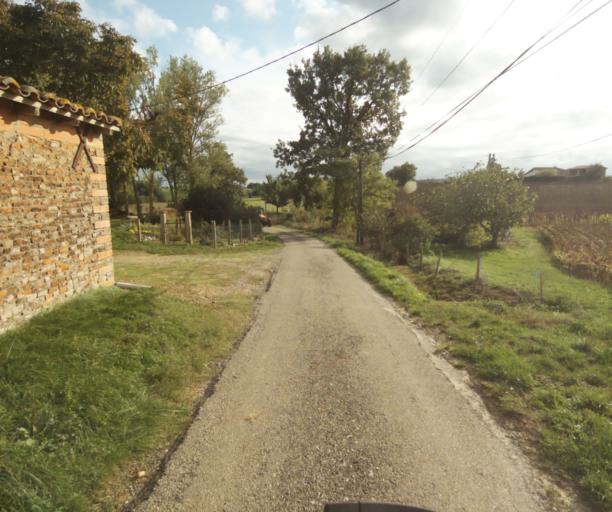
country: FR
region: Midi-Pyrenees
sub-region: Departement du Tarn-et-Garonne
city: Verdun-sur-Garonne
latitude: 43.8410
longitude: 1.1467
